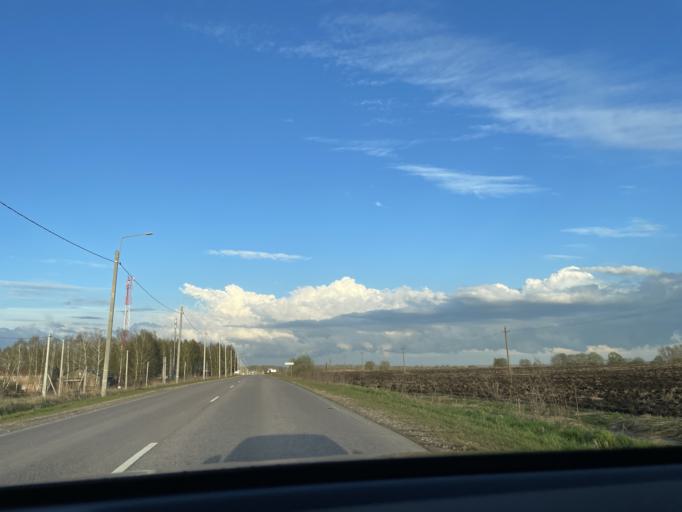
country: RU
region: Tula
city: Novogurovskiy
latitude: 54.5267
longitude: 37.4061
